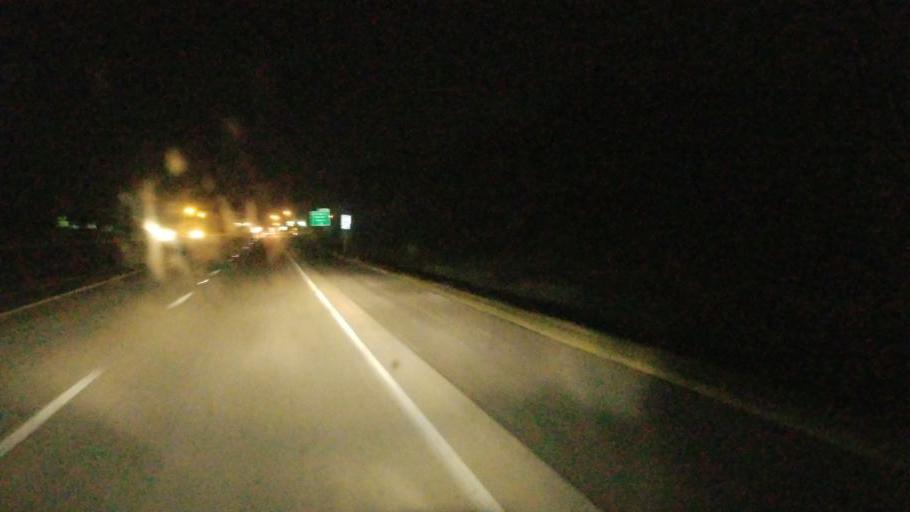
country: US
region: Indiana
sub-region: DeKalb County
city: Auburn
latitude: 41.3200
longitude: -85.0877
